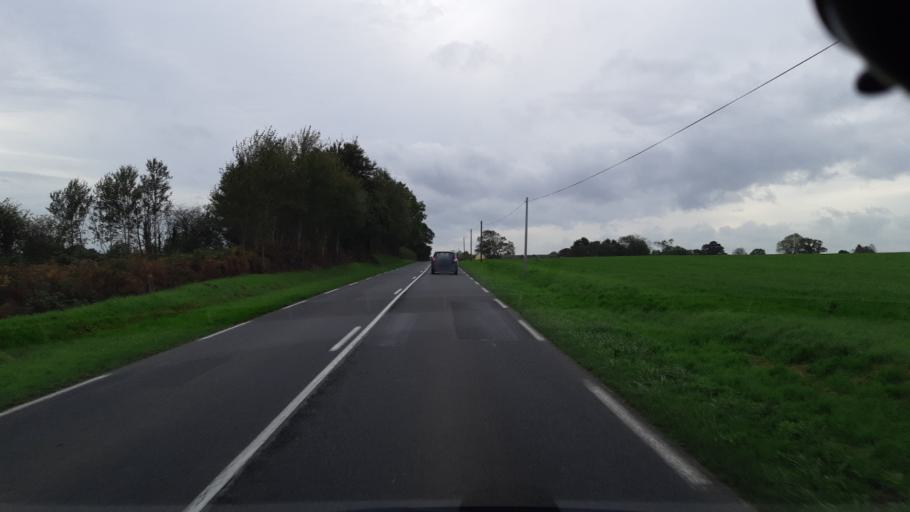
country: FR
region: Lower Normandy
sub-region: Departement de la Manche
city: Gavray
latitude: 48.9361
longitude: -1.3629
